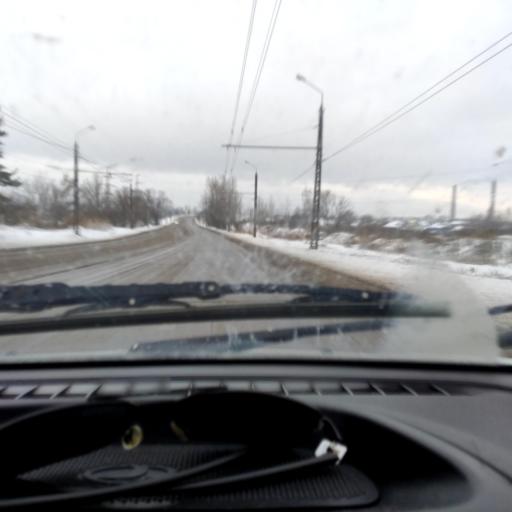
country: RU
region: Samara
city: Zhigulevsk
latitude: 53.4937
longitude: 49.5046
